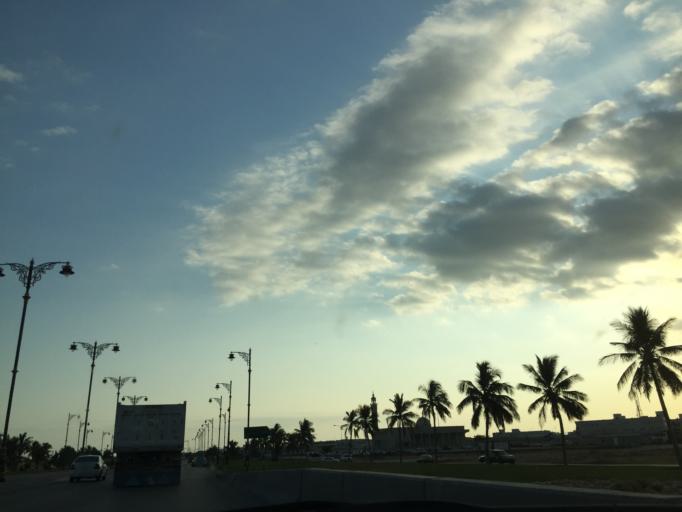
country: OM
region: Zufar
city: Salalah
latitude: 17.0253
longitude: 54.0581
